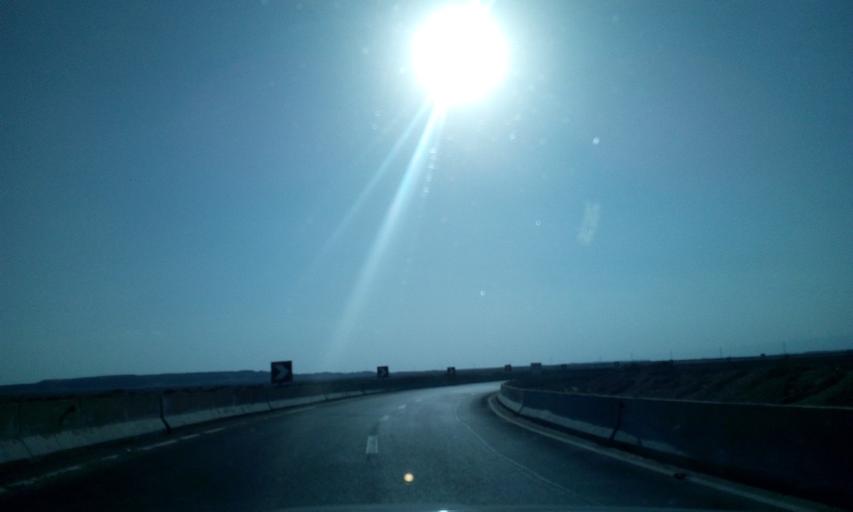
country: EG
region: As Suways
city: Ain Sukhna
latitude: 29.1055
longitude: 32.5326
